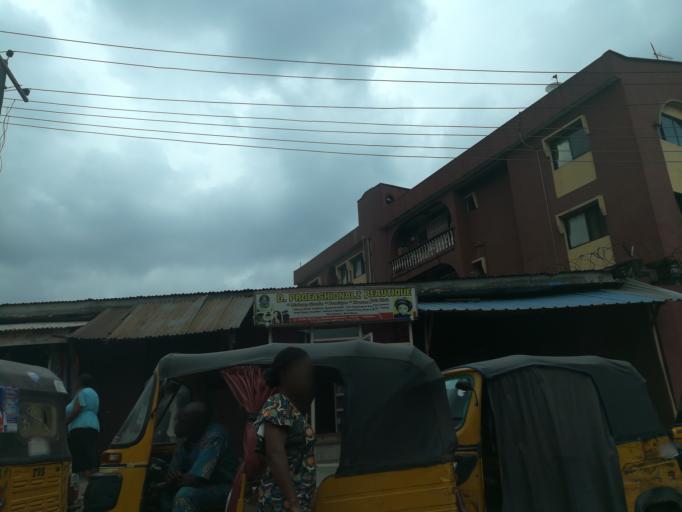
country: NG
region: Lagos
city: Ojota
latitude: 6.6070
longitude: 3.3996
